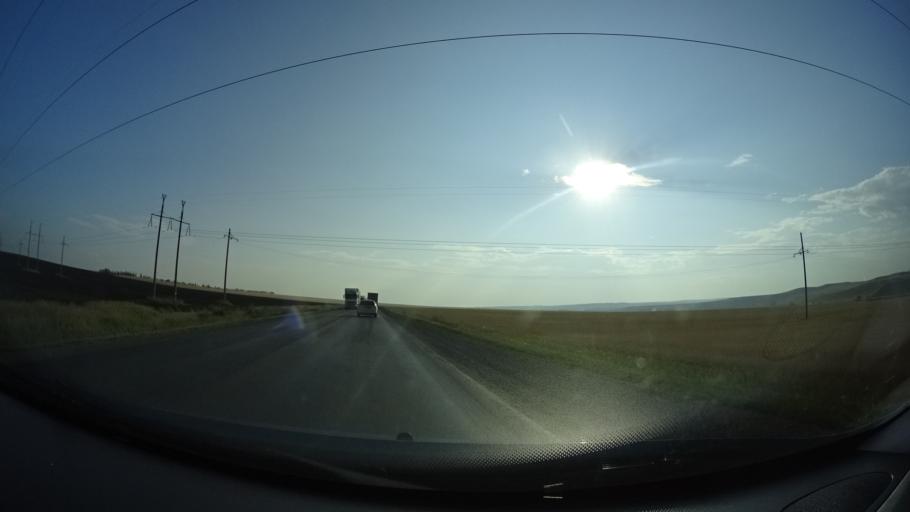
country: RU
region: Orenburg
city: Severnoye
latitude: 54.1270
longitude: 52.5699
